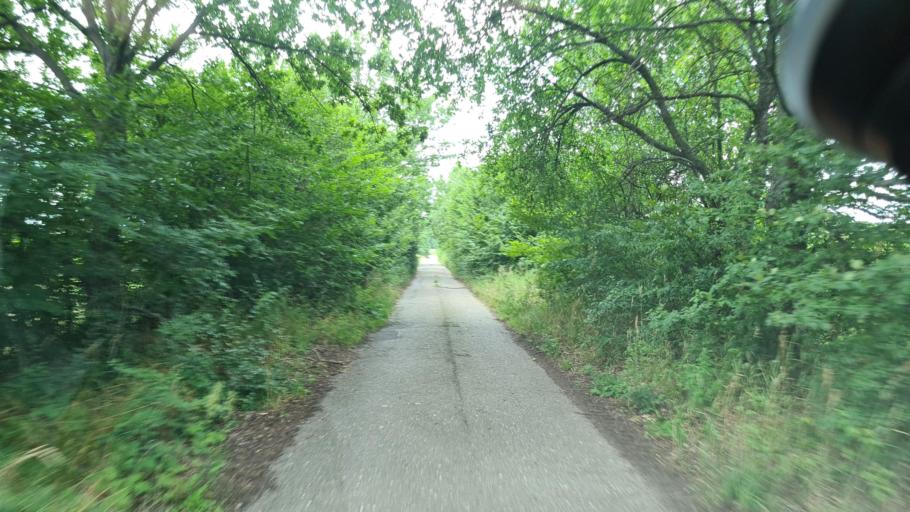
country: DE
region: Brandenburg
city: Drebkau
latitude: 51.6353
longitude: 14.2908
